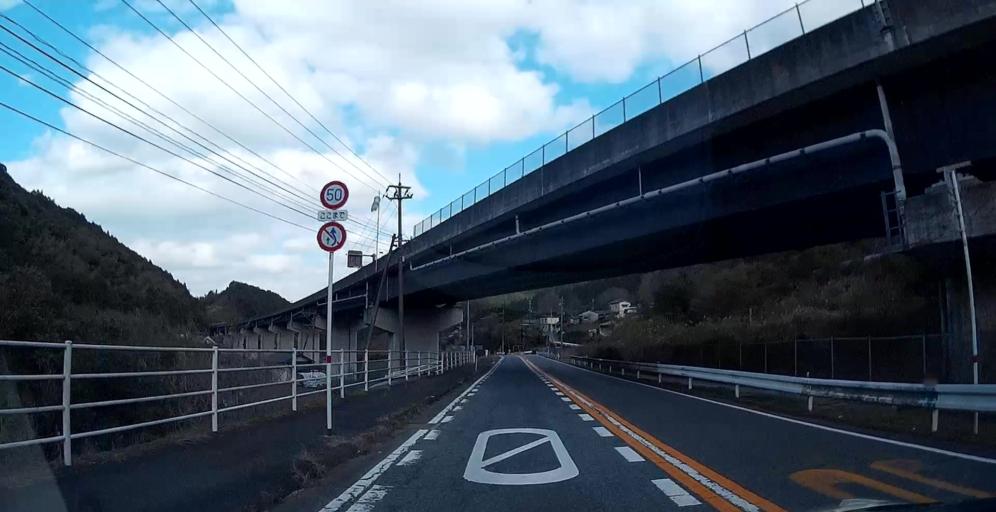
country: JP
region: Kumamoto
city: Yatsushiro
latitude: 32.3827
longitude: 130.5403
